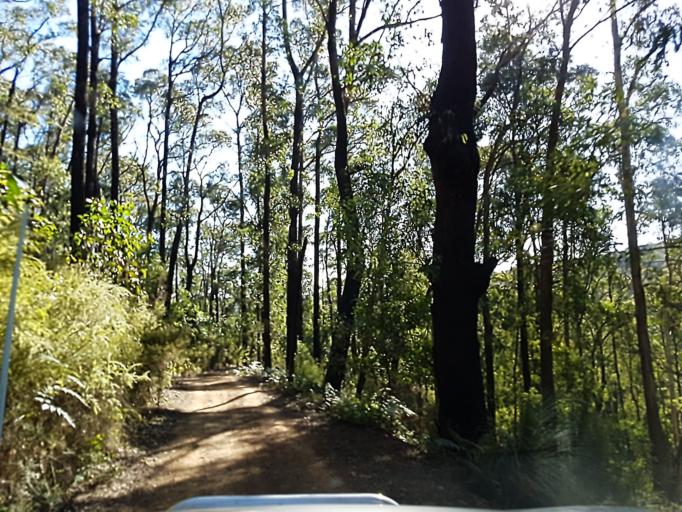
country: AU
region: Victoria
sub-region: Yarra Ranges
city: Healesville
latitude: -37.5653
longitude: 145.4890
